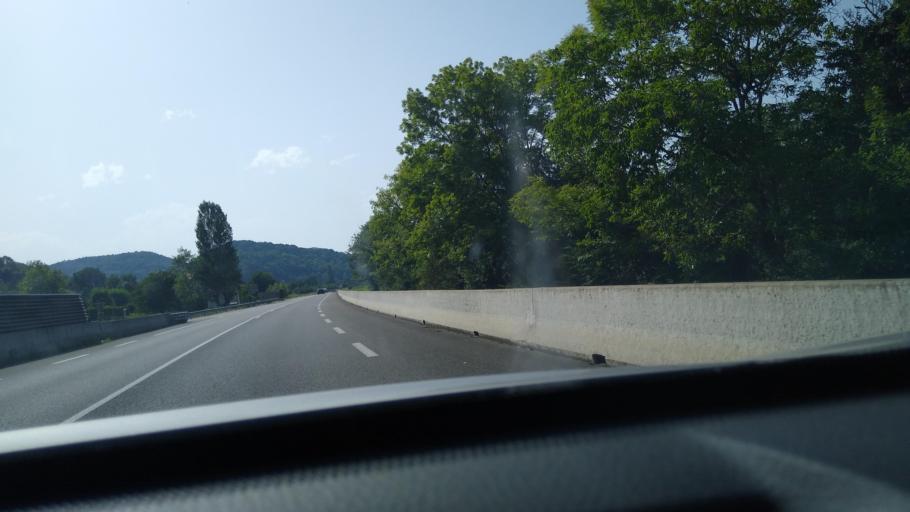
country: FR
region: Midi-Pyrenees
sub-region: Departement de la Haute-Garonne
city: Salies-du-Salat
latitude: 43.0320
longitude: 1.0140
